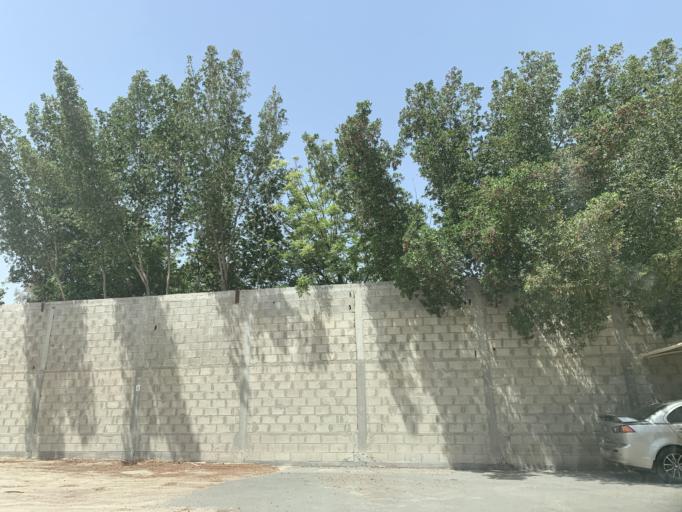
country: BH
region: Northern
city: Ar Rifa'
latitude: 26.1540
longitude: 50.5825
